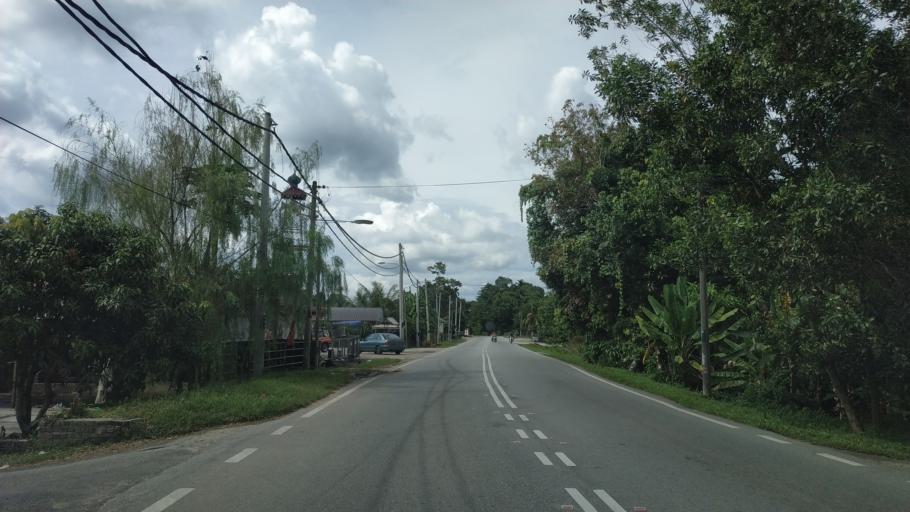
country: MY
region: Kedah
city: Kulim
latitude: 5.4259
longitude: 100.6628
